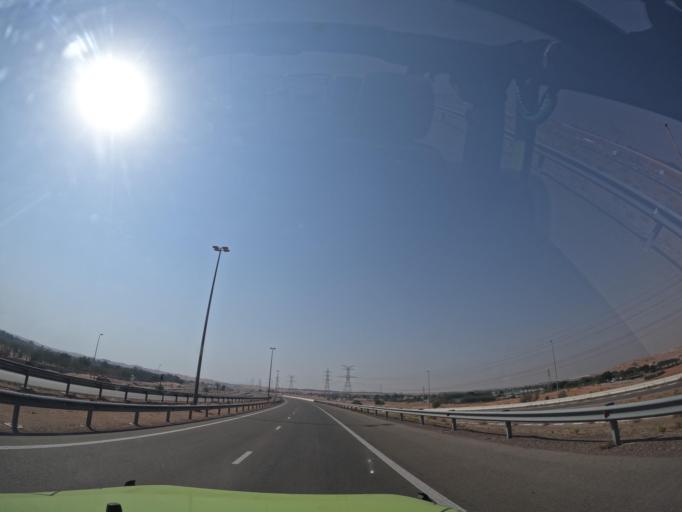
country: OM
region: Al Buraimi
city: Al Buraymi
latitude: 24.3678
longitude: 55.7285
